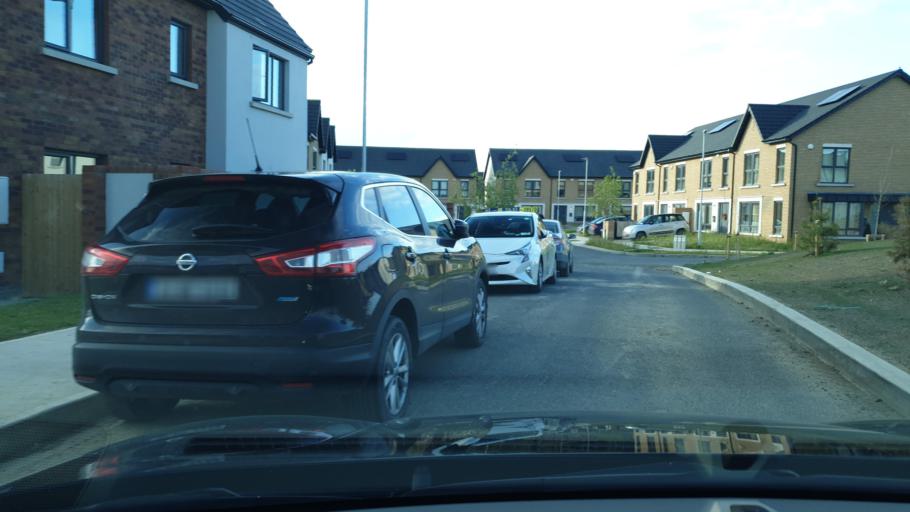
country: IE
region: Leinster
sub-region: Fingal County
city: Blanchardstown
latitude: 53.4228
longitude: -6.3688
